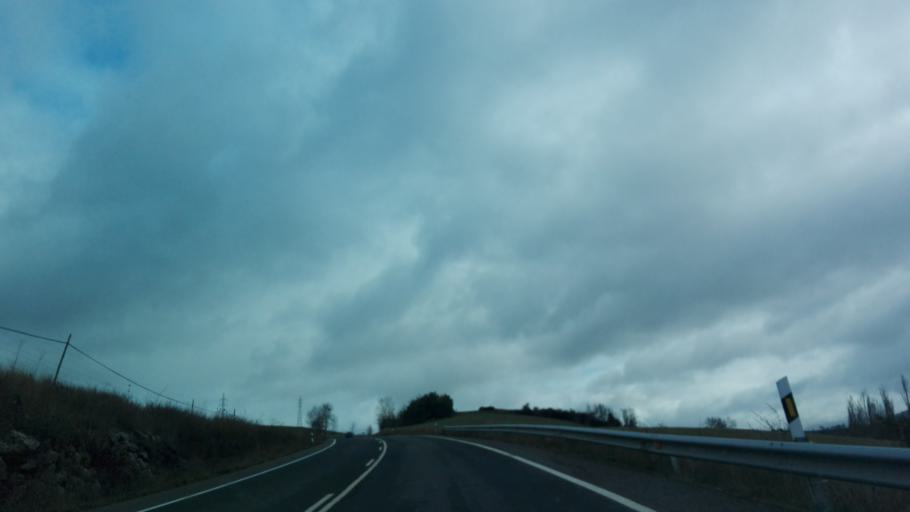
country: ES
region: Navarre
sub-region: Provincia de Navarra
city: Lizoain
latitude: 42.8233
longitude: -1.5231
